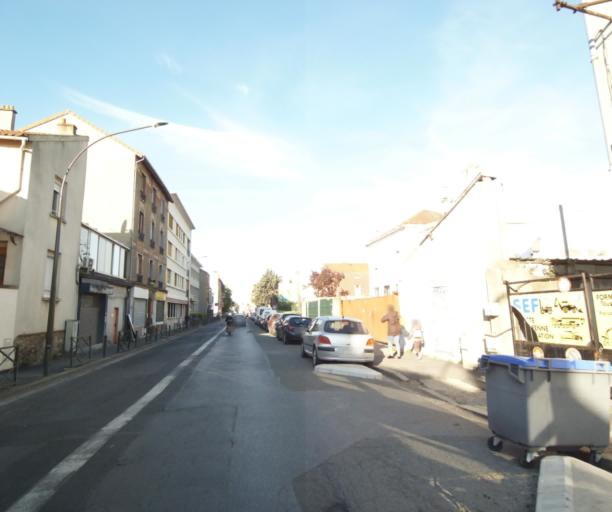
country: FR
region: Ile-de-France
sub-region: Departement du Val-d'Oise
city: Argenteuil
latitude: 48.9375
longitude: 2.2408
